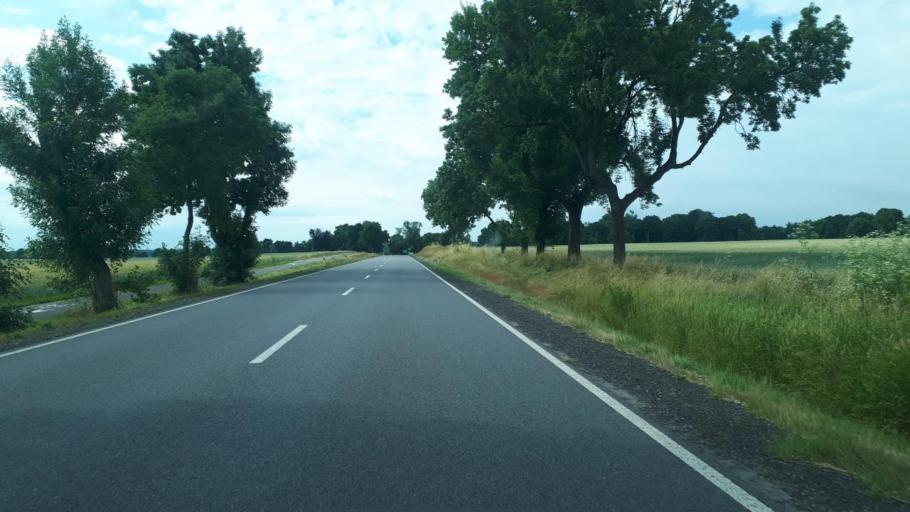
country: PL
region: Opole Voivodeship
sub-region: Powiat oleski
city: Dobrodzien
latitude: 50.7493
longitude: 18.4394
